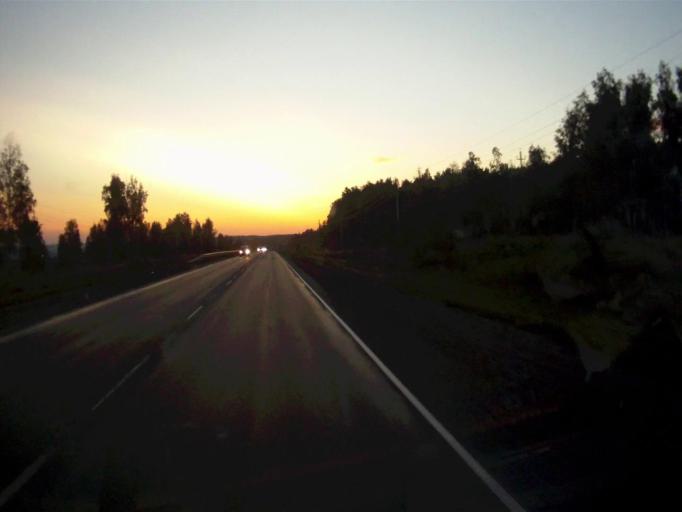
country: RU
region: Chelyabinsk
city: Poletayevo
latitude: 55.2217
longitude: 61.0173
